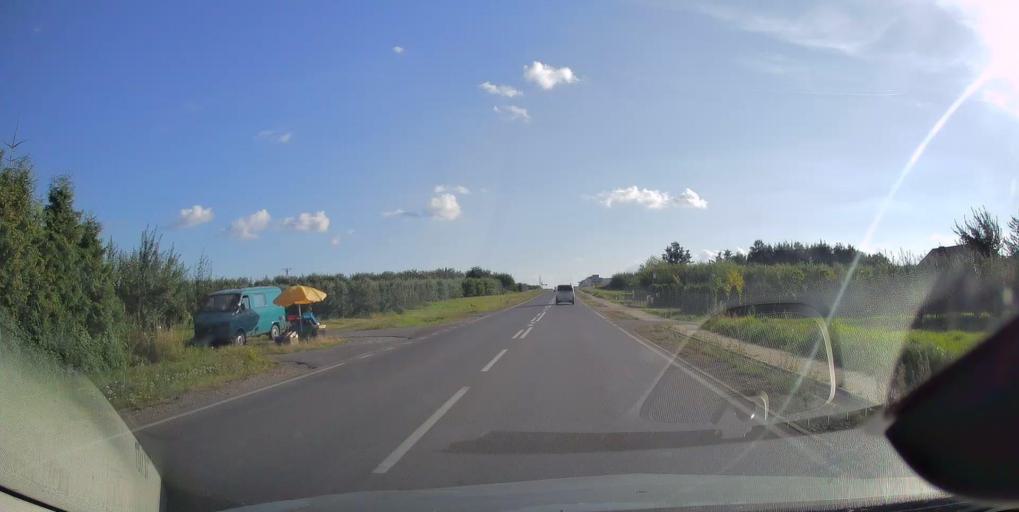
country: PL
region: Masovian Voivodeship
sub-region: Powiat grojecki
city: Belsk Duzy
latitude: 51.8423
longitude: 20.8306
